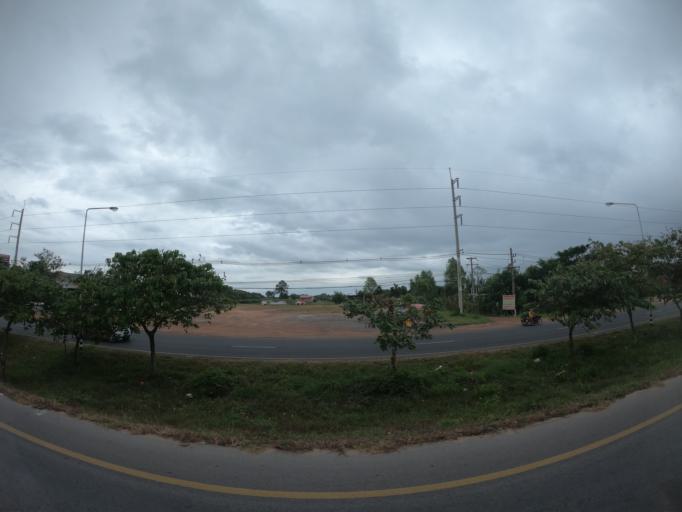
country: TH
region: Roi Et
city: Roi Et
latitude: 16.0525
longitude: 103.6203
